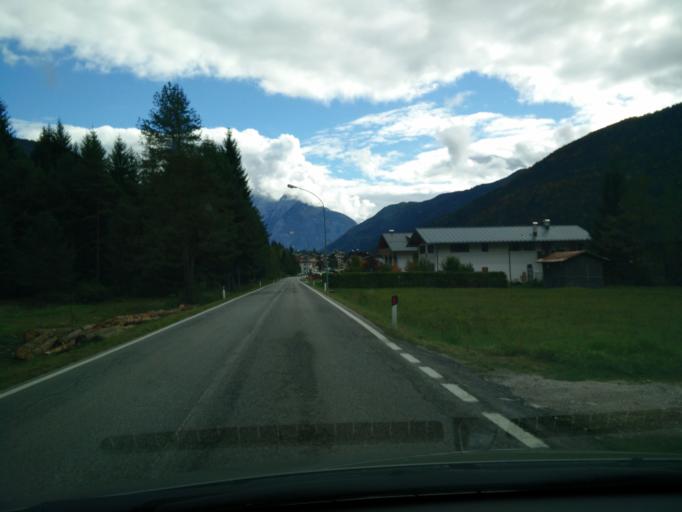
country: IT
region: Veneto
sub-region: Provincia di Belluno
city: Auronzo
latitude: 46.5731
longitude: 12.3950
